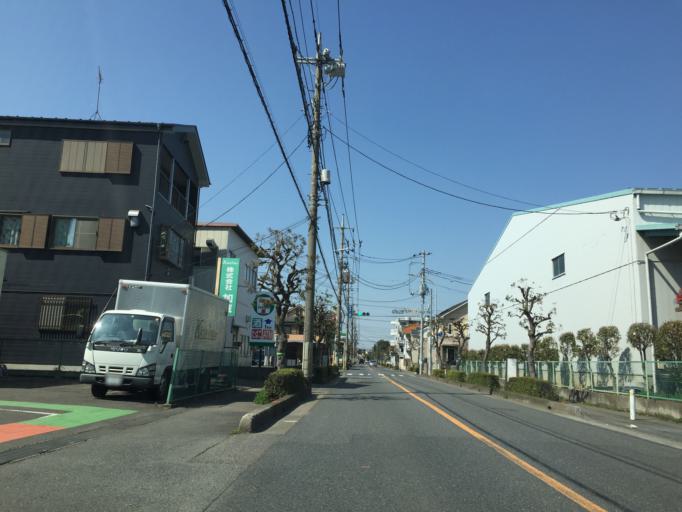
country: JP
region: Saitama
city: Shiki
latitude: 35.8421
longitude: 139.5922
